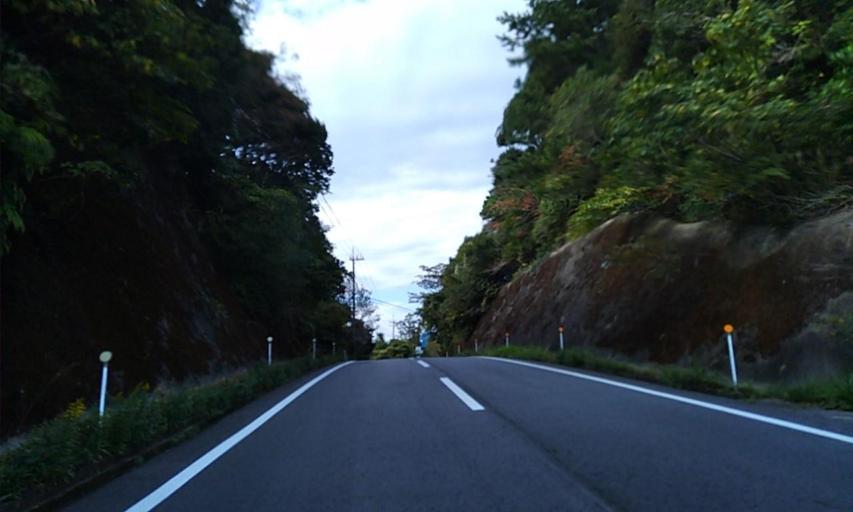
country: JP
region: Wakayama
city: Shingu
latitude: 33.4709
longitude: 135.8186
